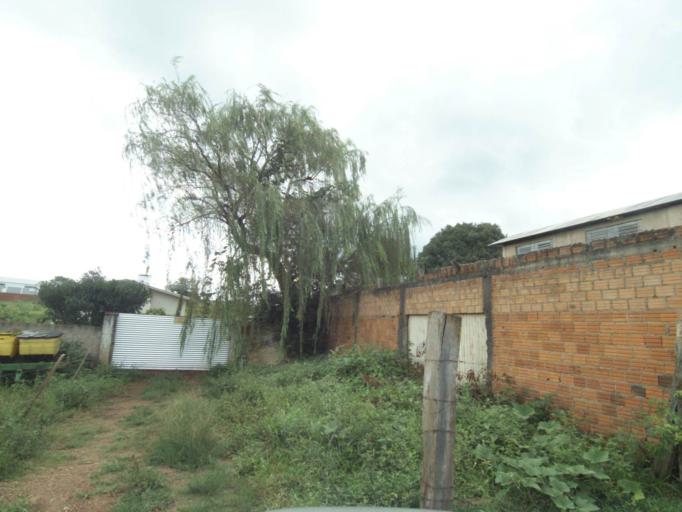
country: BR
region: Rio Grande do Sul
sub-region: Lagoa Vermelha
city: Lagoa Vermelha
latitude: -28.2097
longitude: -51.5431
